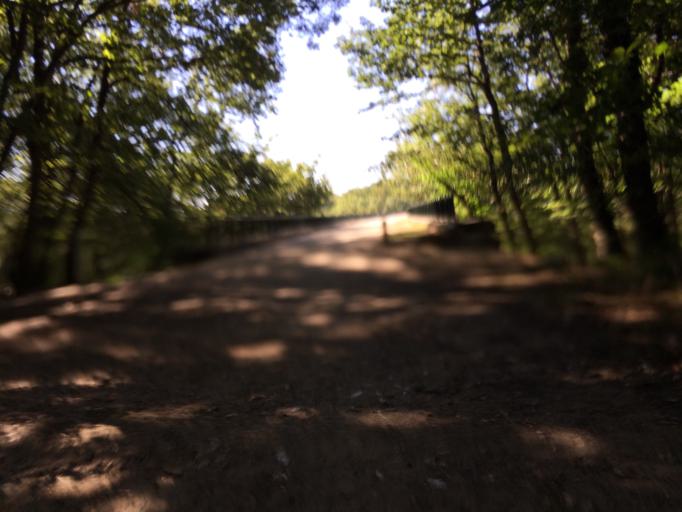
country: FR
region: Ile-de-France
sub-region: Departement de l'Essonne
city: Gometz-le-Chatel
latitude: 48.6800
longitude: 2.1533
